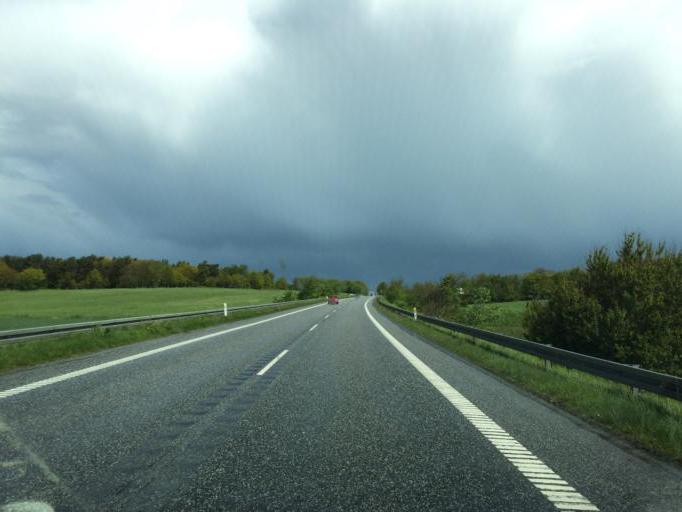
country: DK
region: Central Jutland
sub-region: Skive Kommune
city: Hojslev
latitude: 56.5623
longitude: 9.1116
